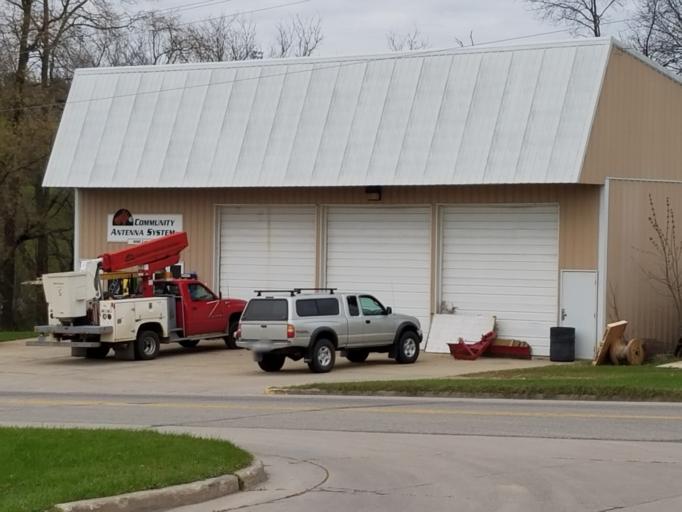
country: US
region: Wisconsin
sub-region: Vernon County
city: Hillsboro
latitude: 43.6522
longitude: -90.3503
